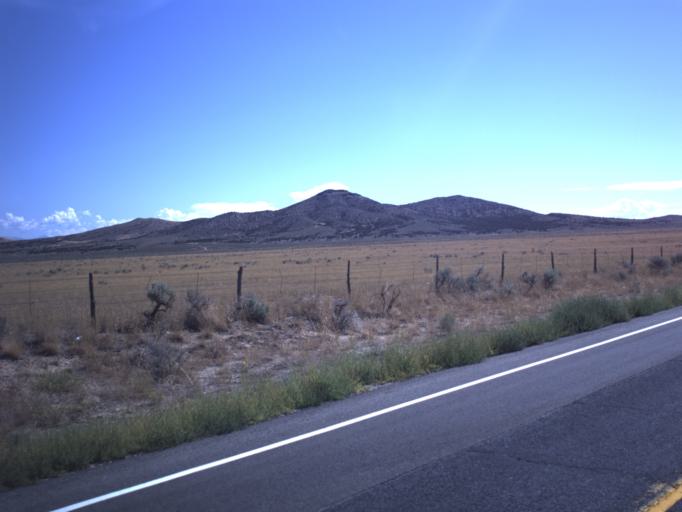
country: US
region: Utah
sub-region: Tooele County
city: Tooele
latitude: 40.0862
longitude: -112.4257
